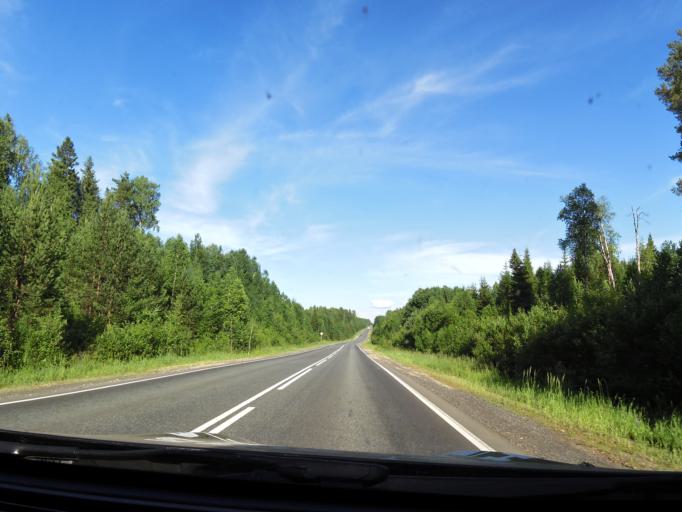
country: RU
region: Kirov
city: Chernaya Kholunitsa
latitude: 58.8727
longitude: 51.5178
